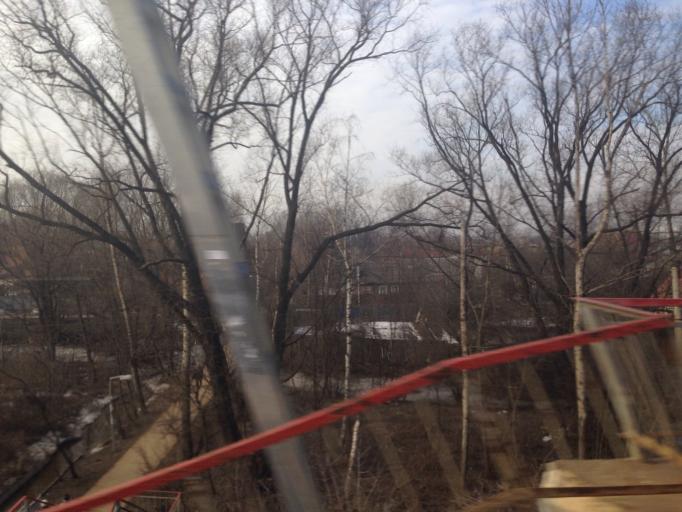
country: RU
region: Moskovskaya
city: Sheremet'yevskiy
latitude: 55.9698
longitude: 37.5049
